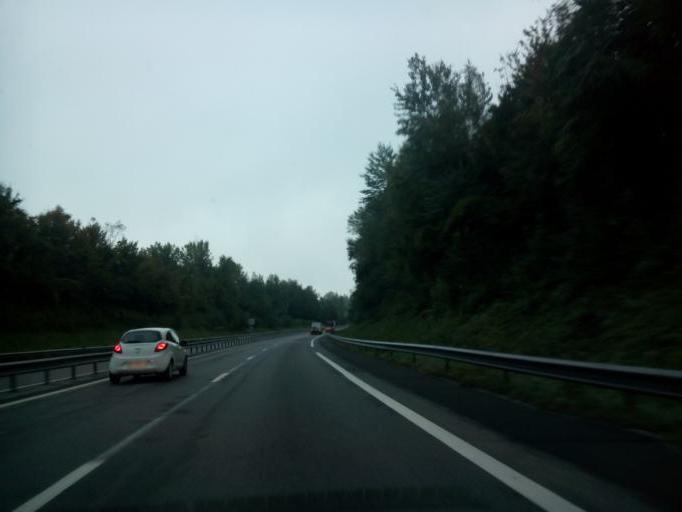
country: FR
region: Rhone-Alpes
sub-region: Departement de la Savoie
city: La Bridoire
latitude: 45.5585
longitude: 5.7586
